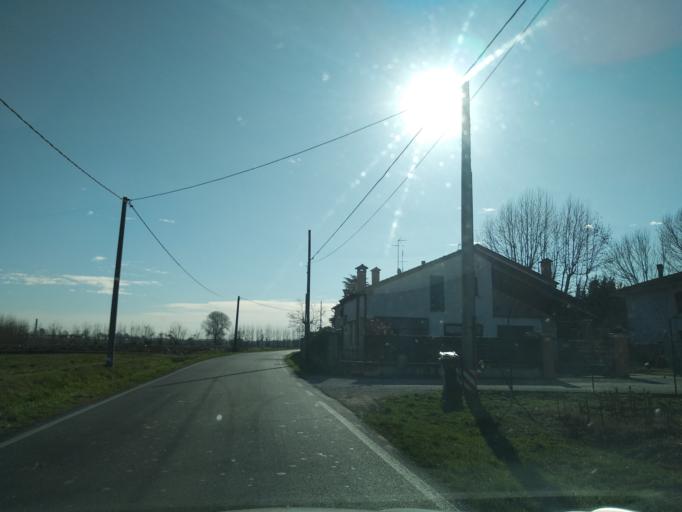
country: IT
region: Veneto
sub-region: Provincia di Padova
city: Bosco
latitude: 45.4549
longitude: 11.7893
